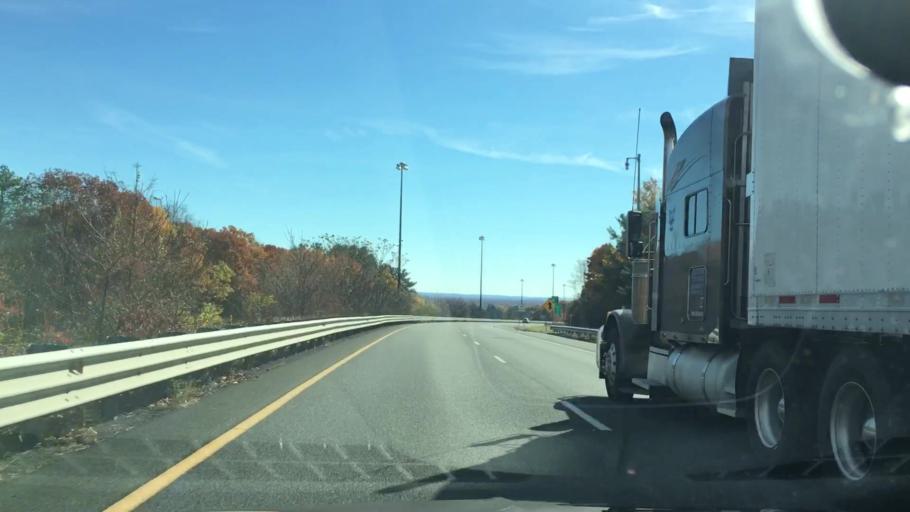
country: US
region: Massachusetts
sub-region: Hampden County
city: Holyoke
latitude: 42.2190
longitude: -72.6341
